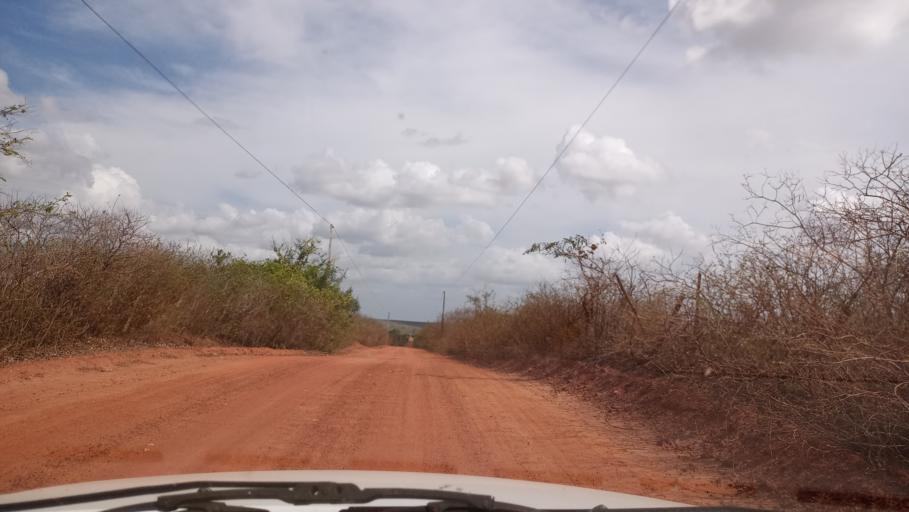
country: BR
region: Rio Grande do Norte
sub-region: Joao Camara
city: Joao Camara
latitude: -5.4595
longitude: -35.8373
